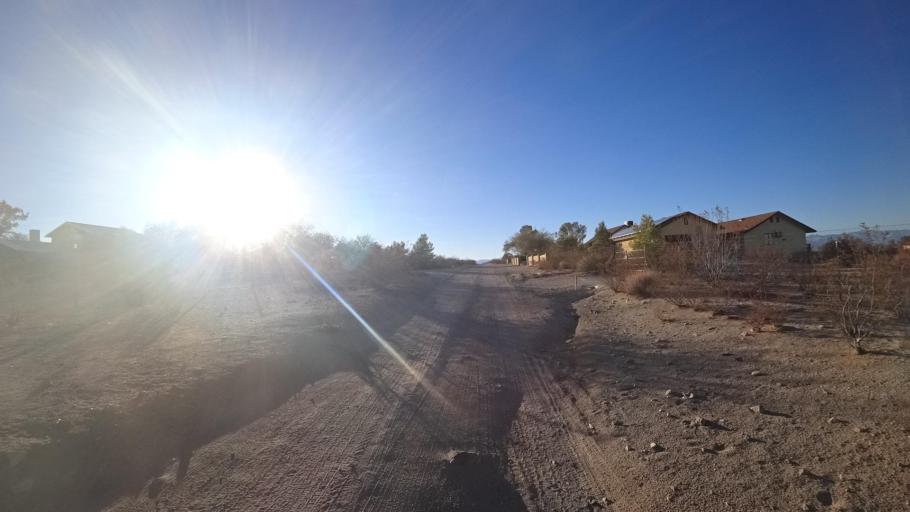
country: US
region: California
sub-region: Kern County
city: Ridgecrest
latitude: 35.5824
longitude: -117.6580
